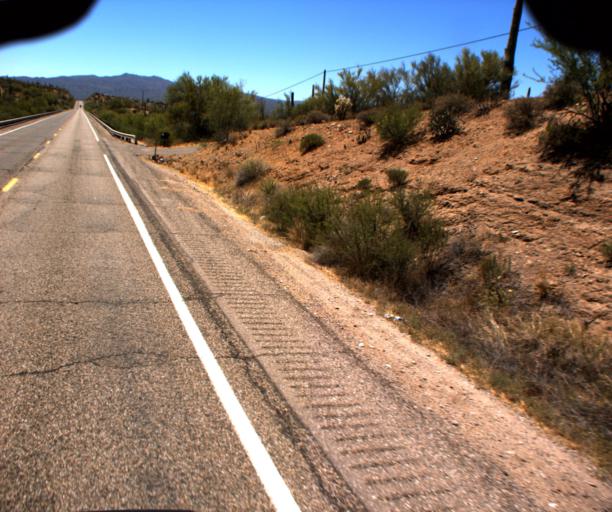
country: US
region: Arizona
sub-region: Pinal County
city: Kearny
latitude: 33.0934
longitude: -110.9309
